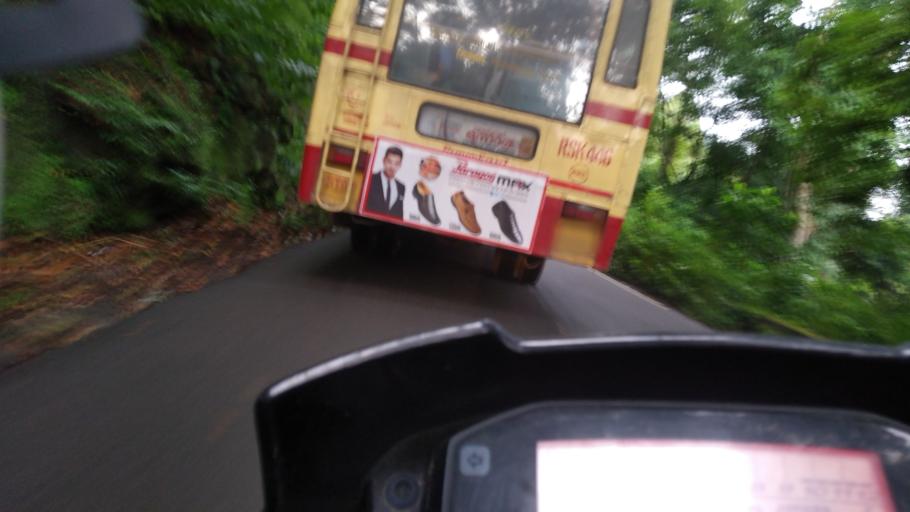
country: IN
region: Kerala
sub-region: Idukki
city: Kuttampuzha
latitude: 10.0665
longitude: 76.7761
